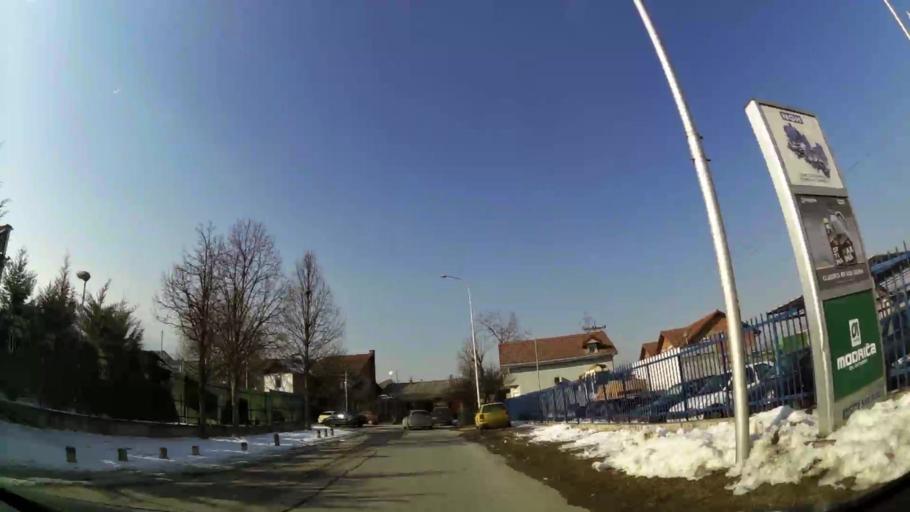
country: MK
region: Kisela Voda
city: Usje
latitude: 41.9715
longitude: 21.4535
